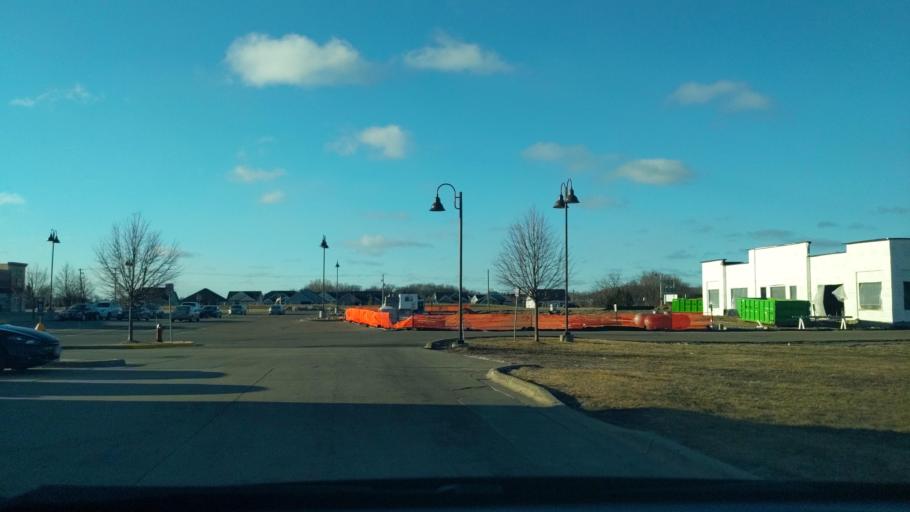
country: US
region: Minnesota
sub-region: Carver County
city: Chanhassen
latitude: 44.8424
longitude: -93.5402
